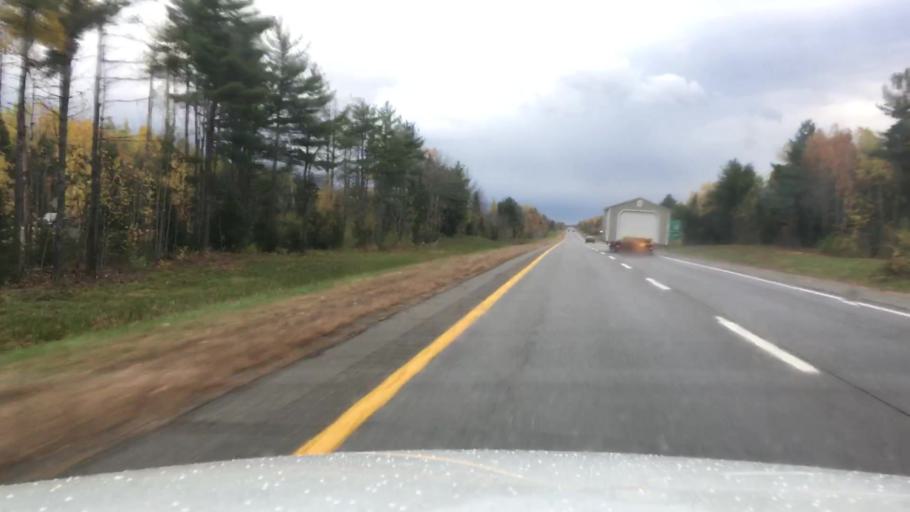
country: US
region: Maine
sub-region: Penobscot County
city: Howland
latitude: 45.2591
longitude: -68.6807
